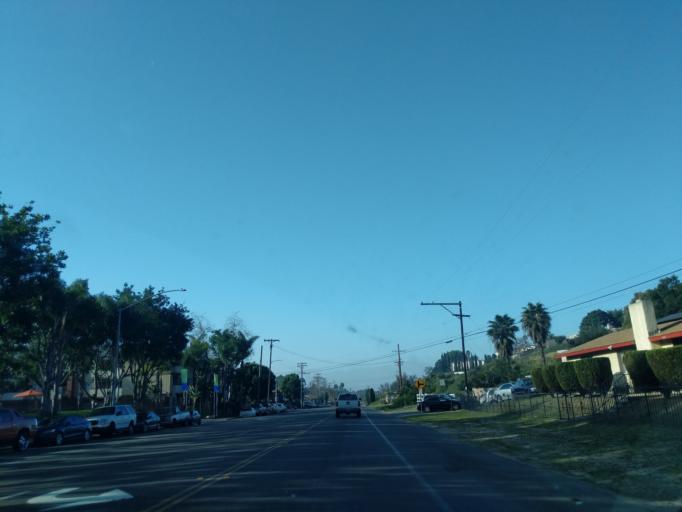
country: US
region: California
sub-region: San Diego County
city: National City
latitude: 32.7333
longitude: -117.0950
